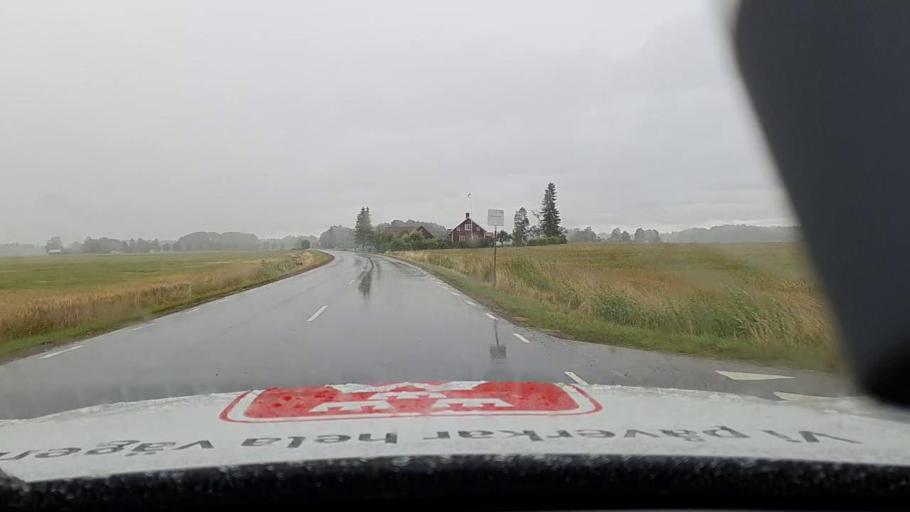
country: SE
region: Vaestra Goetaland
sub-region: Toreboda Kommun
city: Toereboda
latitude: 58.6647
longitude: 14.1299
